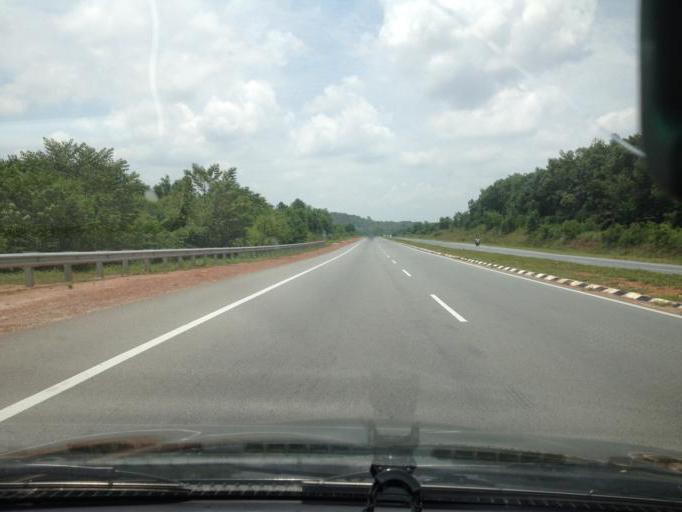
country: MY
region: Kedah
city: Sungai Petani
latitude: 5.6120
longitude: 100.5641
